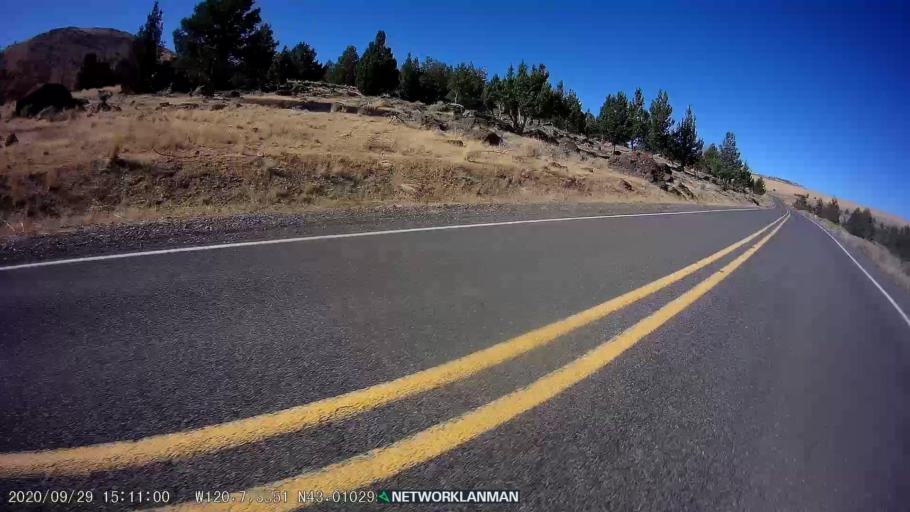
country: US
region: Oregon
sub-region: Lake County
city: Lakeview
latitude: 43.0105
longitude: -120.7735
